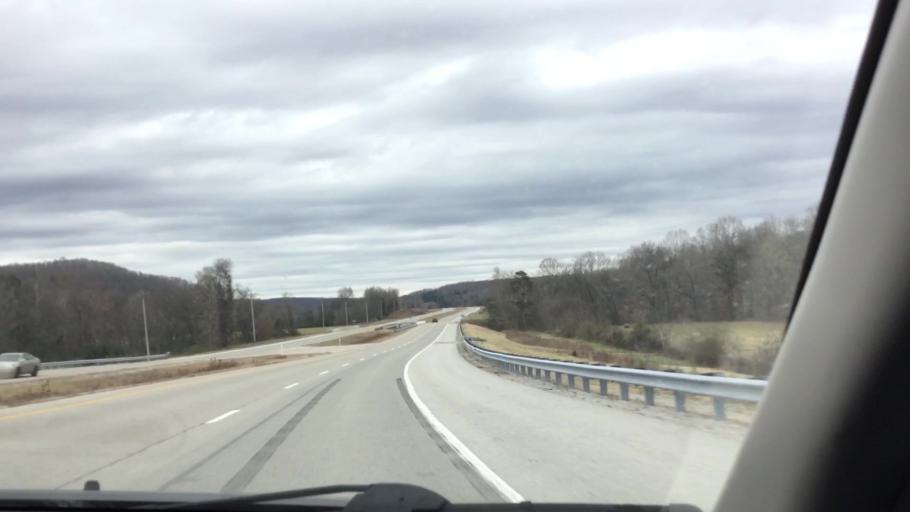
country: US
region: Tennessee
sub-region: Lewis County
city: Hohenwald
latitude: 35.5910
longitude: -87.4514
